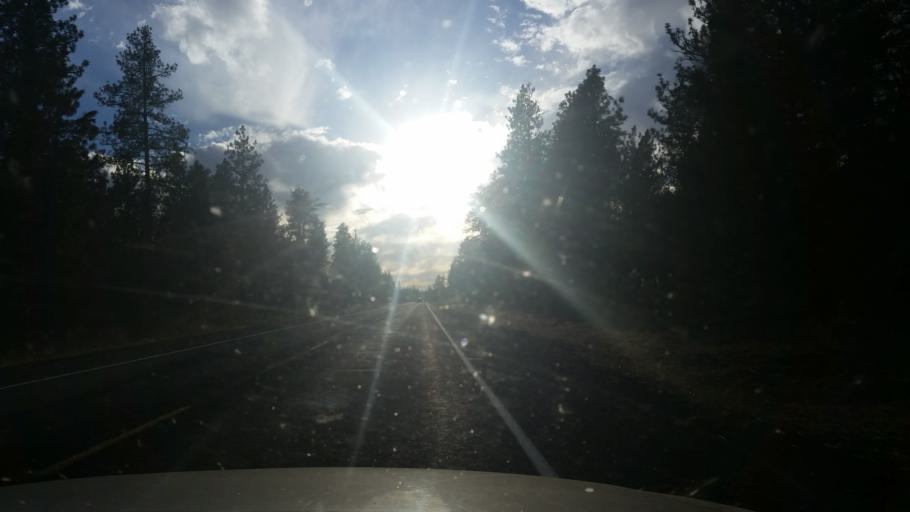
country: US
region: Washington
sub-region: Spokane County
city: Medical Lake
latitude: 47.4499
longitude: -117.7173
